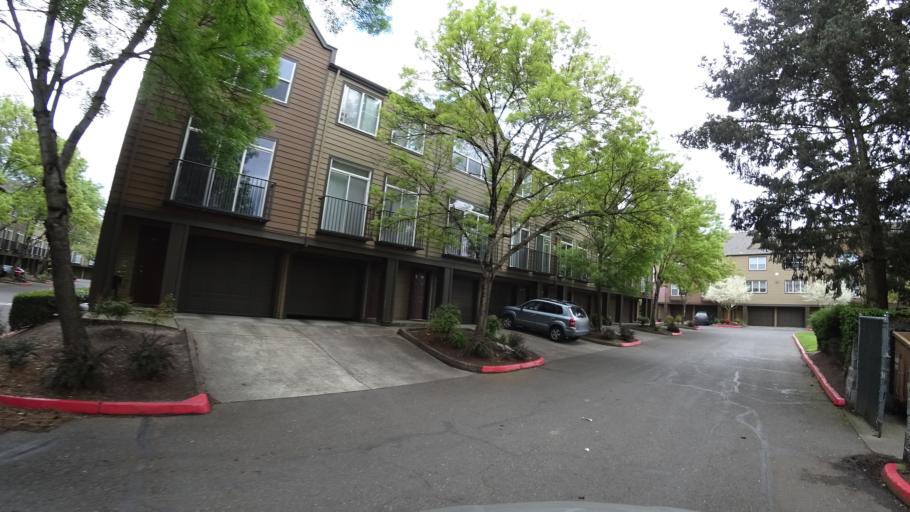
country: US
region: Oregon
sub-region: Washington County
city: Rockcreek
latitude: 45.5422
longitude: -122.8862
